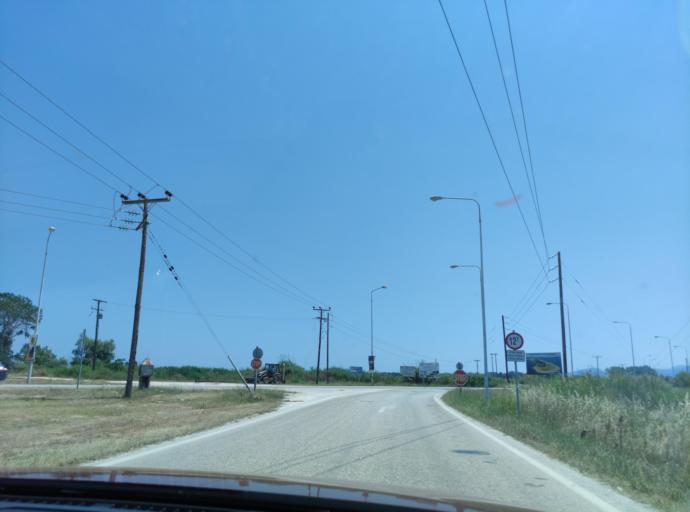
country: GR
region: East Macedonia and Thrace
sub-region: Nomos Kavalas
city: Keramoti
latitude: 40.8683
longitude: 24.7047
